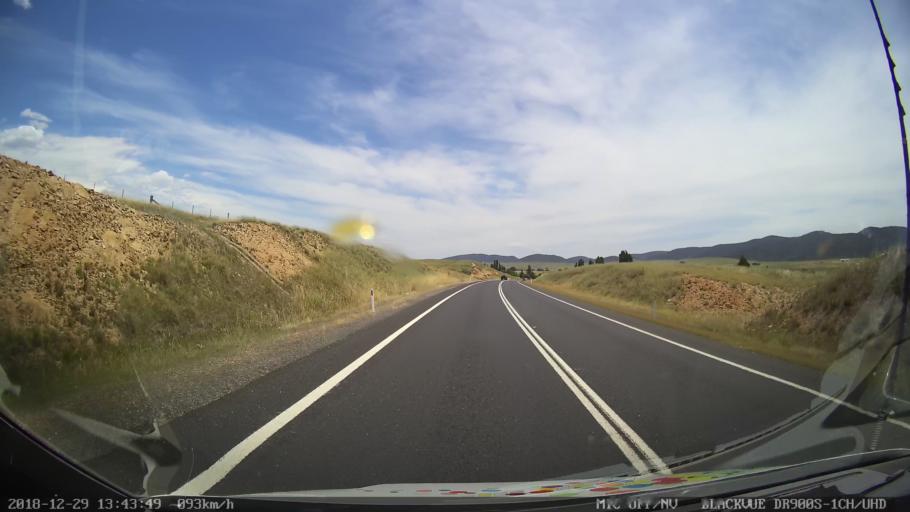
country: AU
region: New South Wales
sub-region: Cooma-Monaro
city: Cooma
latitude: -36.0778
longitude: 149.1596
